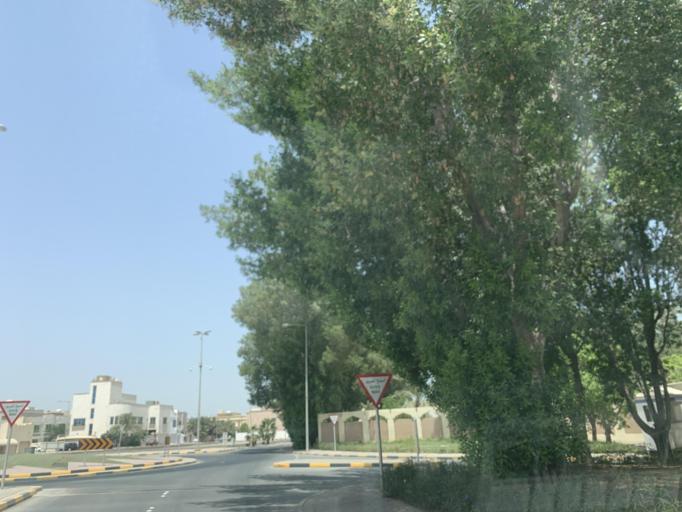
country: BH
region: Northern
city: Madinat `Isa
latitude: 26.1641
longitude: 50.5784
